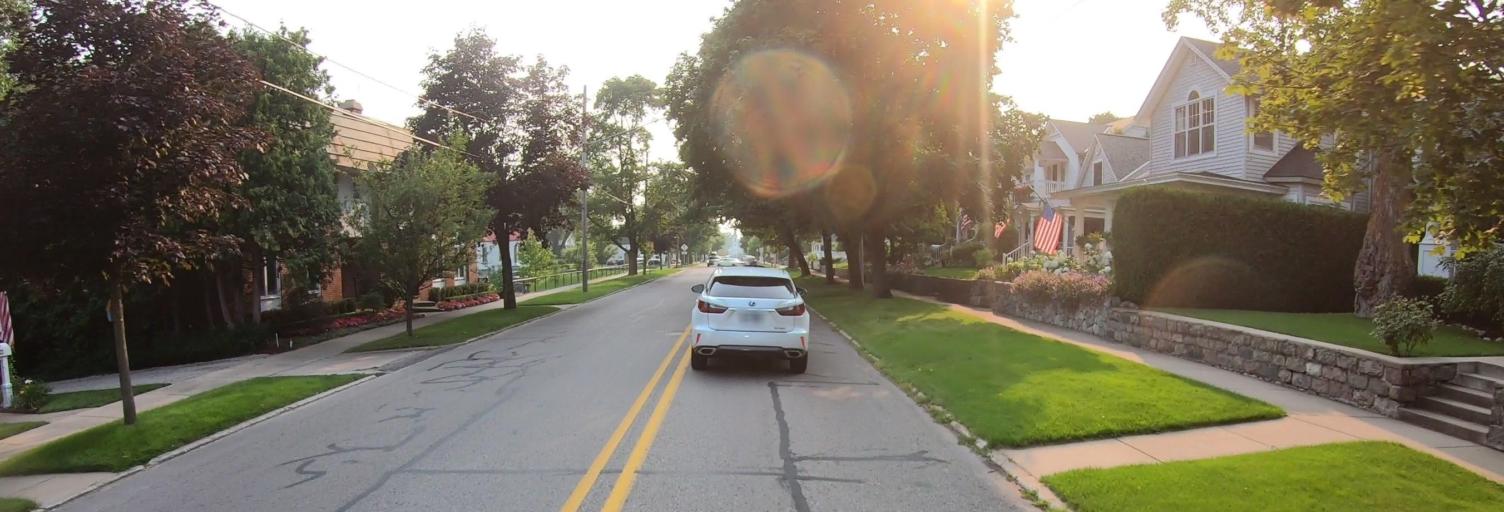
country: US
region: Michigan
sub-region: Emmet County
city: Harbor Springs
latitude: 45.4312
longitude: -84.9831
